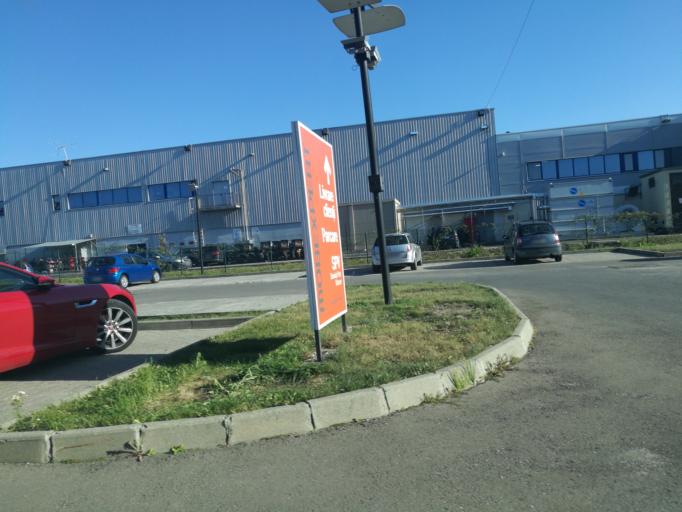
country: RO
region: Brasov
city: Brasov
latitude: 45.6330
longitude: 25.6383
